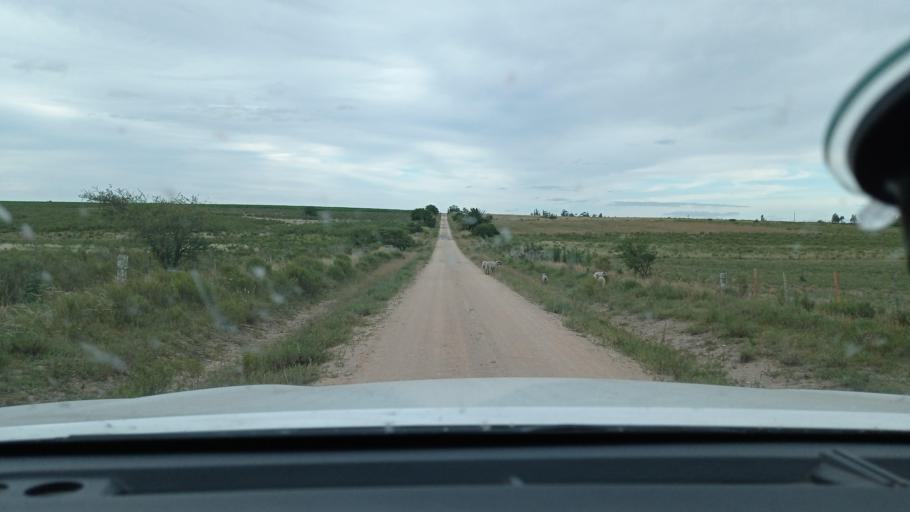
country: UY
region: Florida
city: Casupa
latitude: -34.1365
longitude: -55.7829
